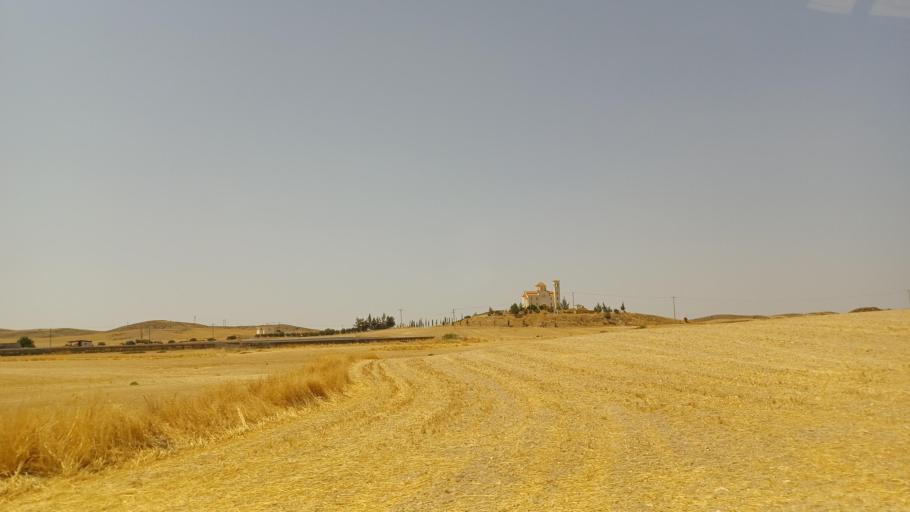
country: CY
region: Larnaka
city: Troulloi
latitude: 35.0306
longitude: 33.5964
